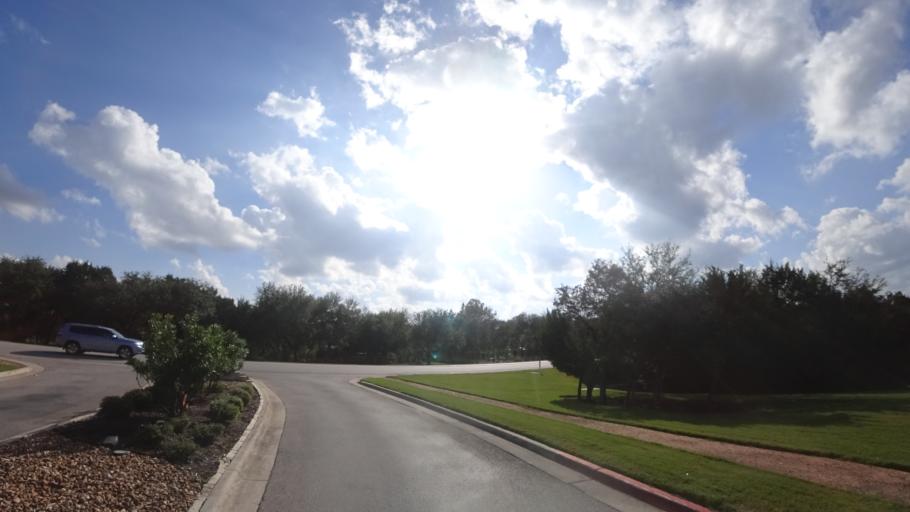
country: US
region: Texas
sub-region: Travis County
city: Barton Creek
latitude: 30.2895
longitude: -97.8681
